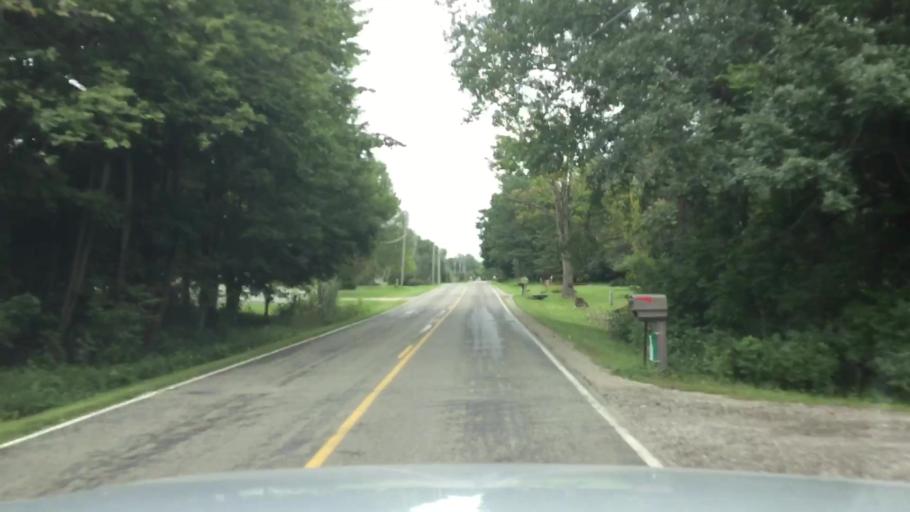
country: US
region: Michigan
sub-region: Shiawassee County
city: Durand
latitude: 42.9516
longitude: -83.9366
